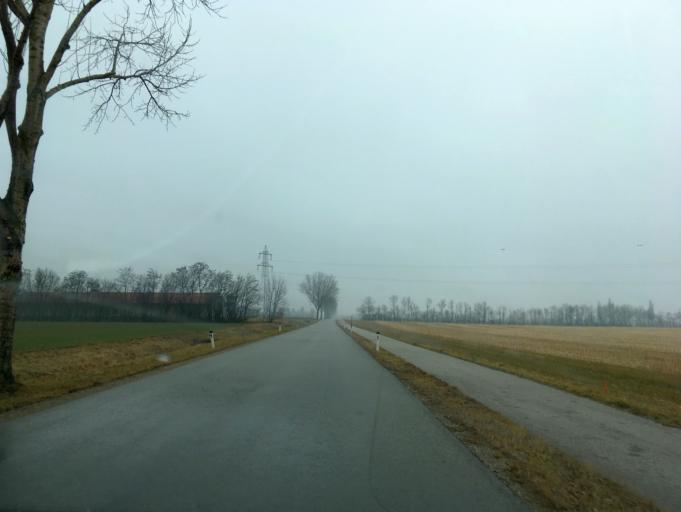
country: AT
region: Lower Austria
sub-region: Politischer Bezirk Bruck an der Leitha
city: Trautmannsdorf an der Leitha
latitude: 48.0502
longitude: 16.6541
